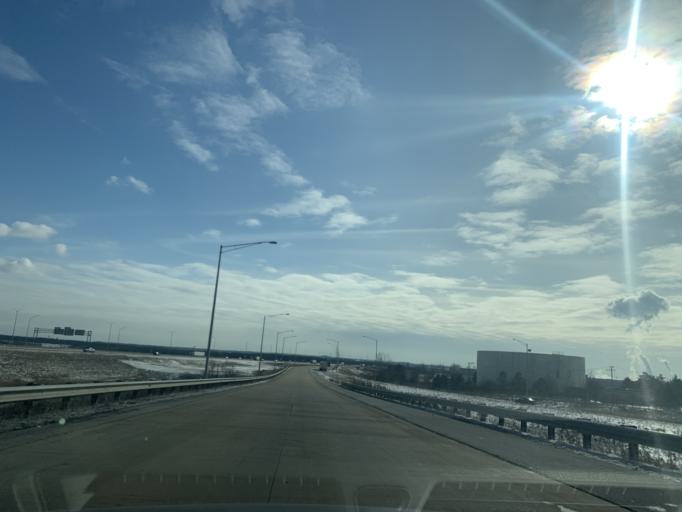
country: US
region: Illinois
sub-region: Will County
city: Bolingbrook
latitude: 41.7022
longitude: -88.0324
